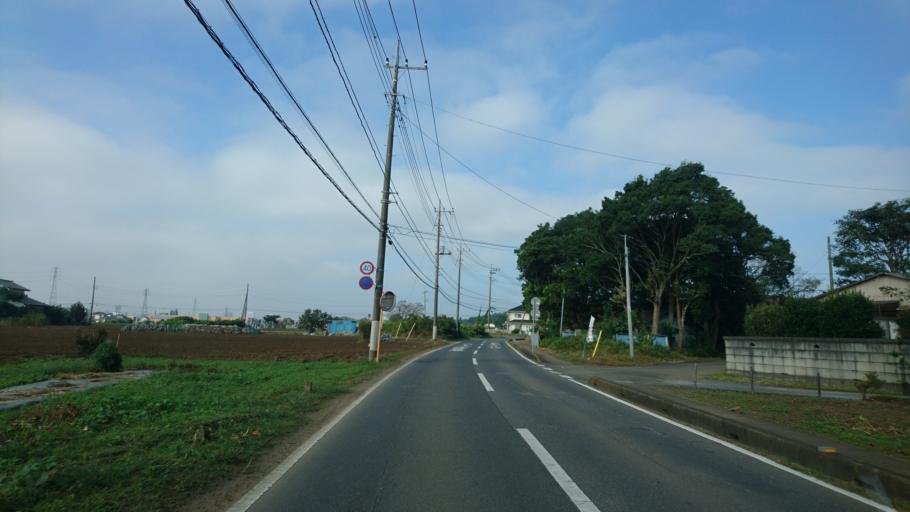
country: JP
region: Ibaraki
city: Naka
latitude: 36.0438
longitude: 140.0922
